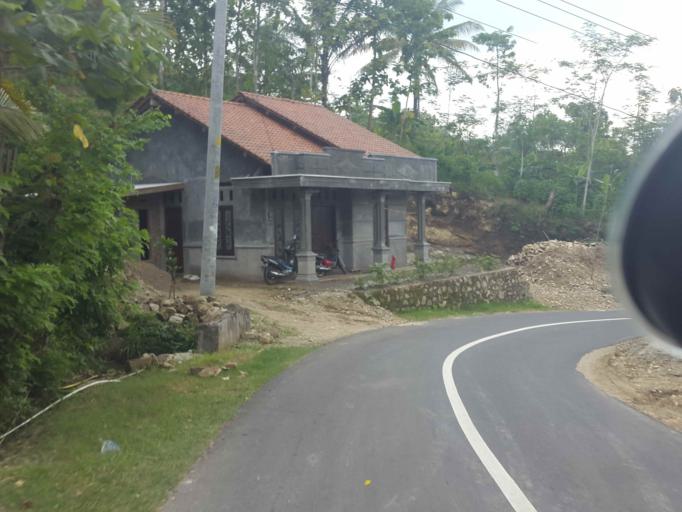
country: ID
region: Central Java
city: Sudikampir
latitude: -7.4230
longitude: 108.9804
